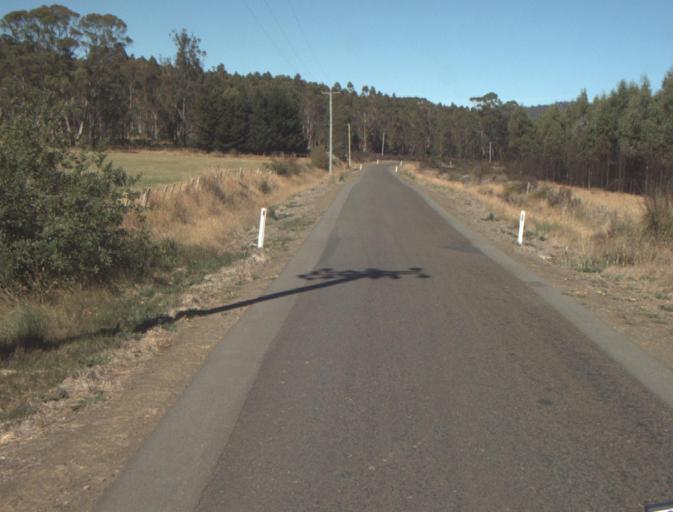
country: AU
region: Tasmania
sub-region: Launceston
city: Newstead
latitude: -41.3238
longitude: 147.3198
